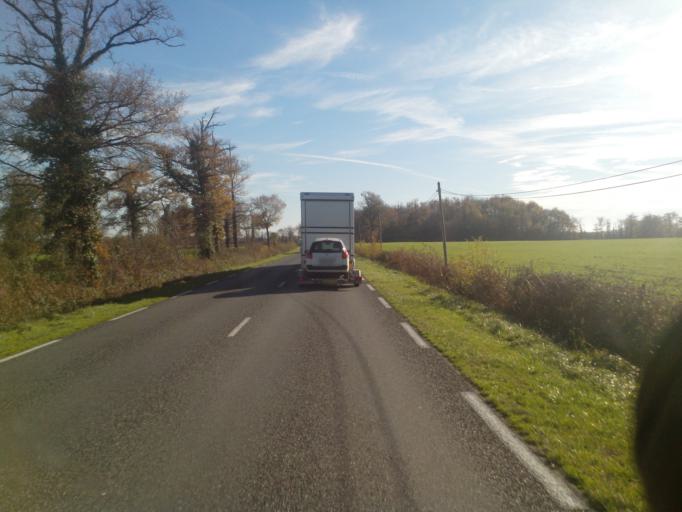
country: FR
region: Limousin
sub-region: Departement de la Haute-Vienne
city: Bellac
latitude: 46.0872
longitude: 1.0835
